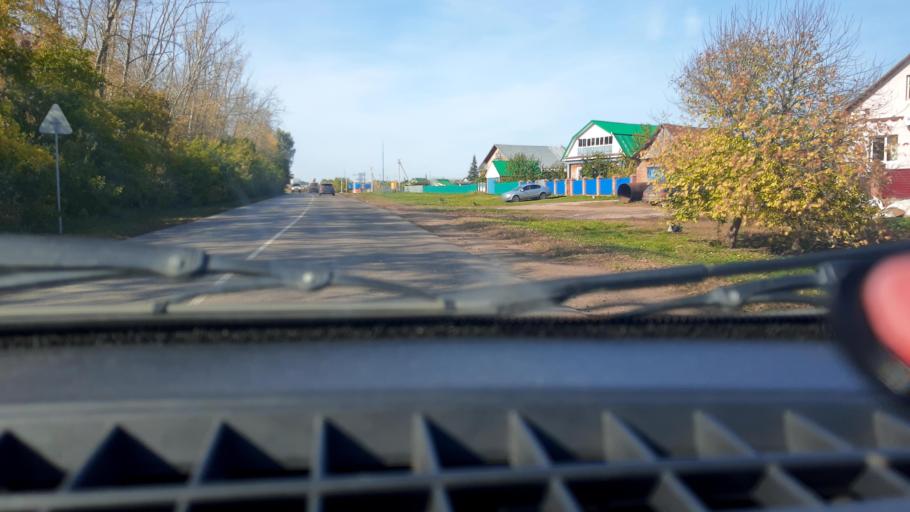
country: RU
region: Bashkortostan
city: Chishmy
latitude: 54.5976
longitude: 55.4470
